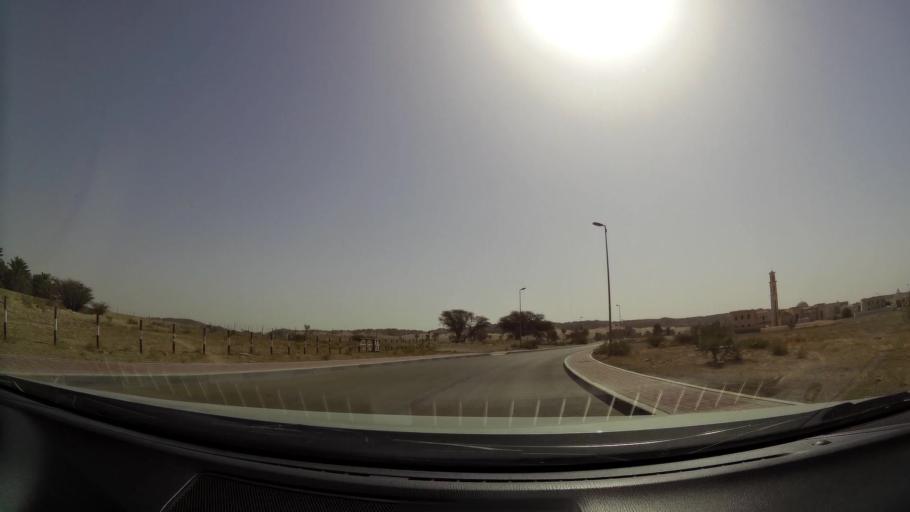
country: OM
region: Al Buraimi
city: Al Buraymi
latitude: 24.3219
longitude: 55.8064
